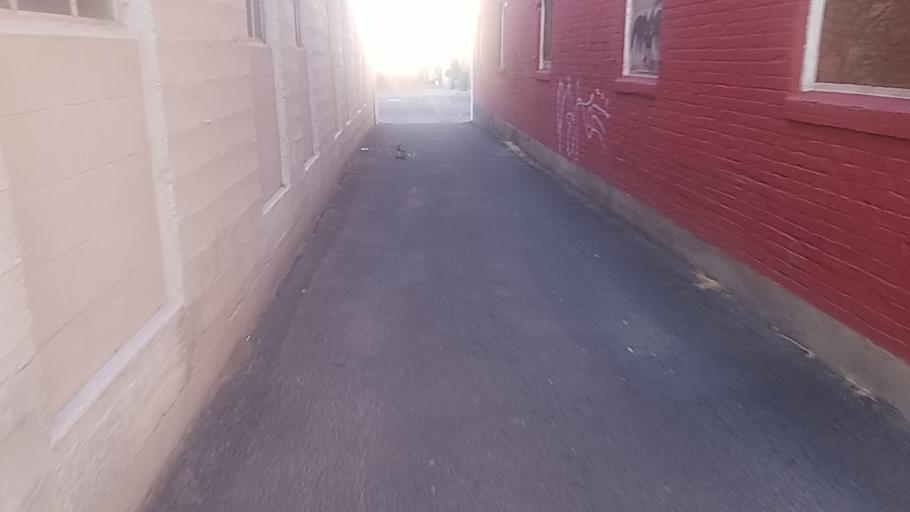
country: US
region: Washington
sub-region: Walla Walla County
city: Walla Walla
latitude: 46.0680
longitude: -118.3381
